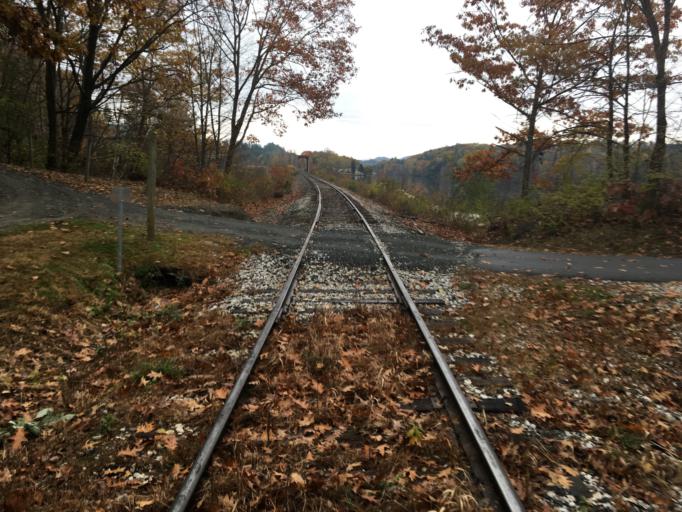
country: US
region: New Hampshire
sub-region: Grafton County
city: Hanover
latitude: 43.7498
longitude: -72.2317
